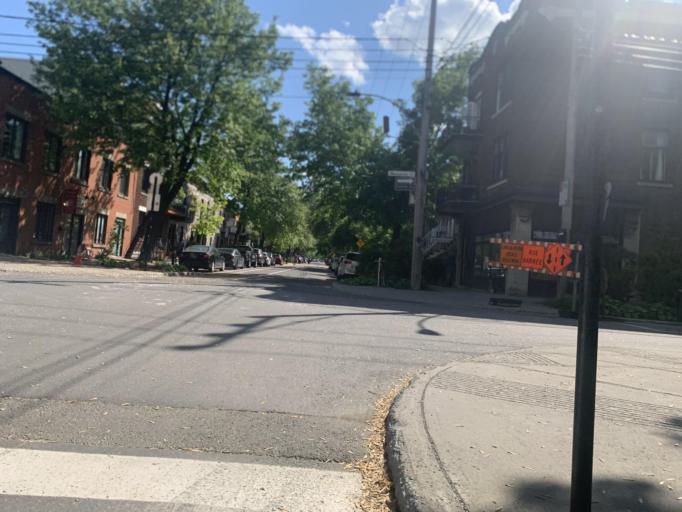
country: CA
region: Quebec
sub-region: Montreal
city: Montreal
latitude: 45.5312
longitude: -73.5729
